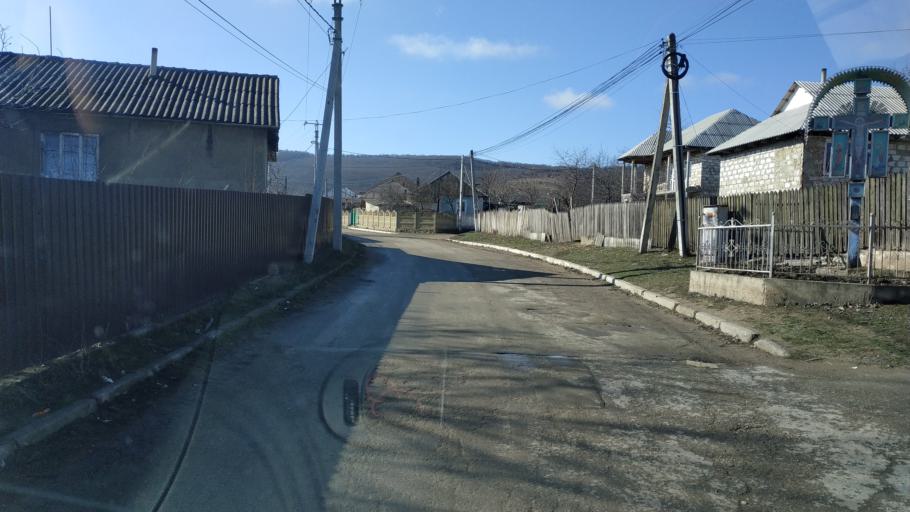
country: MD
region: Hincesti
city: Hincesti
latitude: 46.9223
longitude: 28.6270
